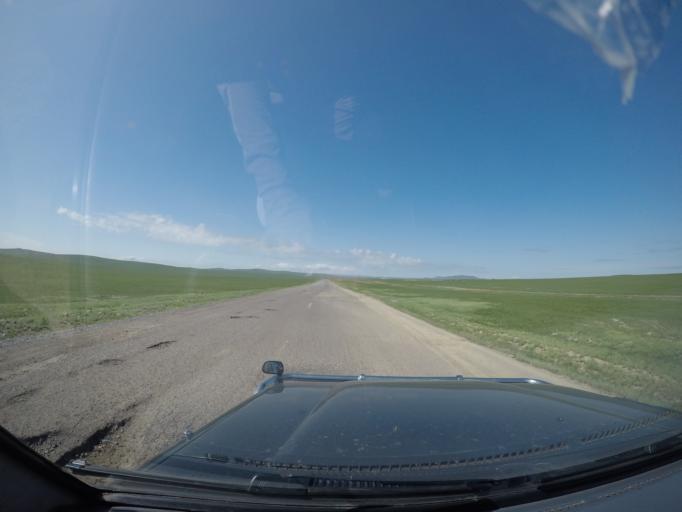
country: MN
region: Suhbaatar
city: Bayasgalant
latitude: 47.3464
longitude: 111.6247
